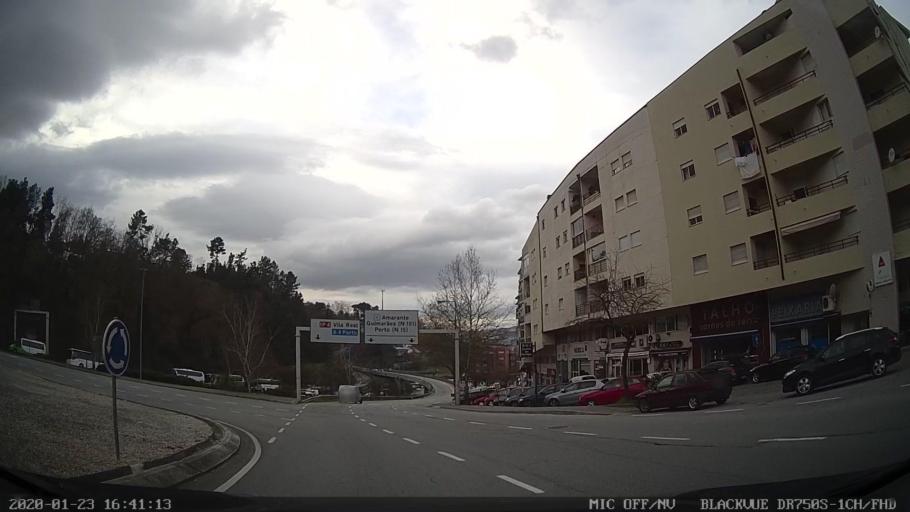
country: PT
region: Porto
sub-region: Amarante
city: Amarante
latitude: 41.2651
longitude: -8.0684
